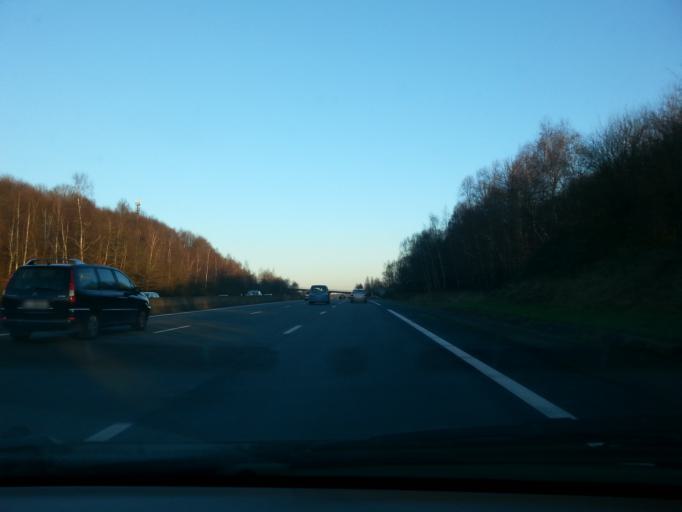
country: FR
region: Centre
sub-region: Departement d'Eure-et-Loir
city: Authon-du-Perche
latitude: 48.1926
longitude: 0.8485
